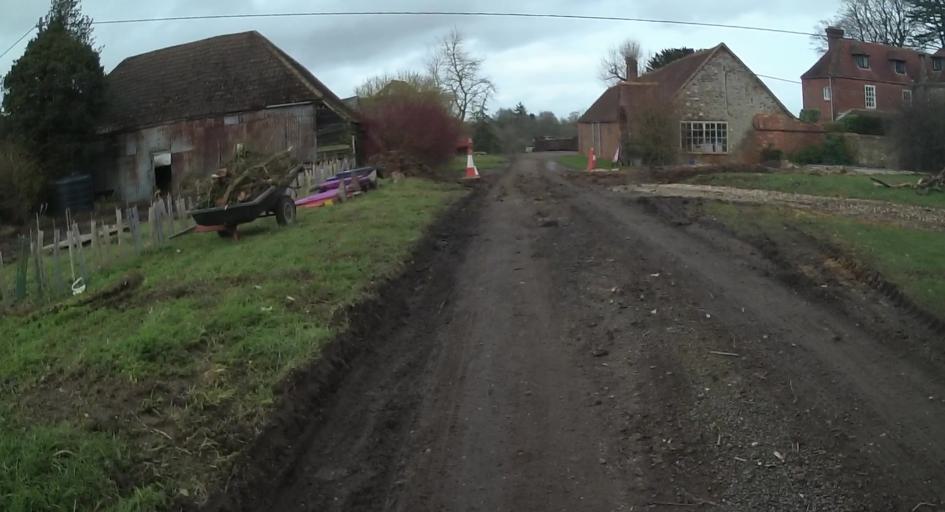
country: GB
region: England
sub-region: Hampshire
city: Kingsclere
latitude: 51.3187
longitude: -1.2199
